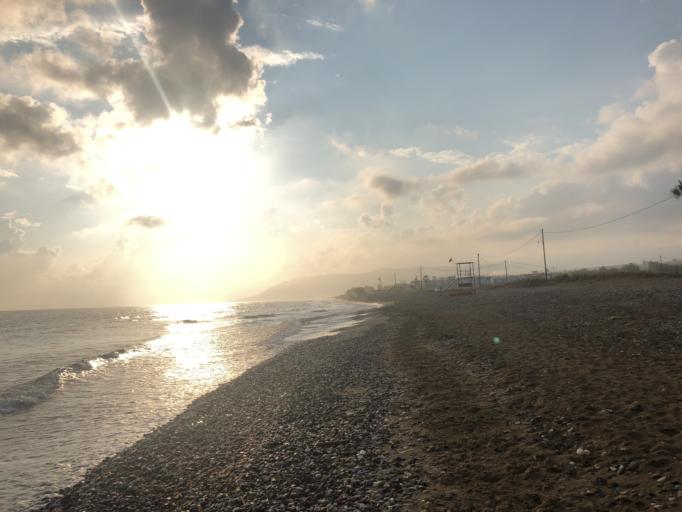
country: GR
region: Crete
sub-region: Nomos Chanias
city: Georgioupolis
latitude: 35.3532
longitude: 24.3031
